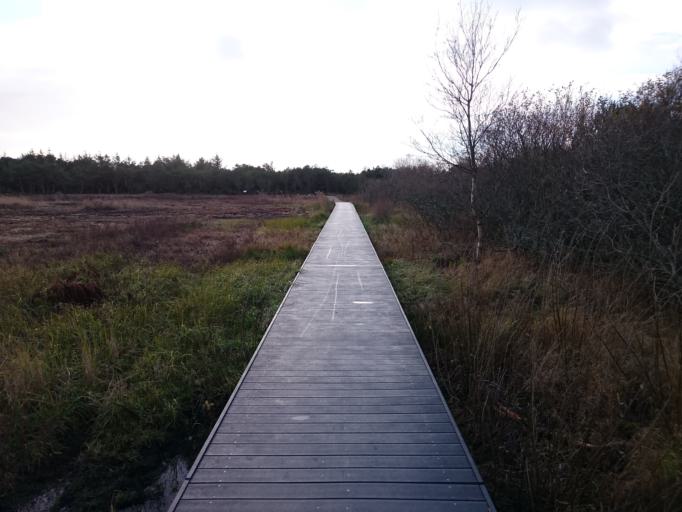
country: DK
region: North Denmark
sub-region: Frederikshavn Kommune
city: Skagen
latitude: 57.7383
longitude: 10.6172
